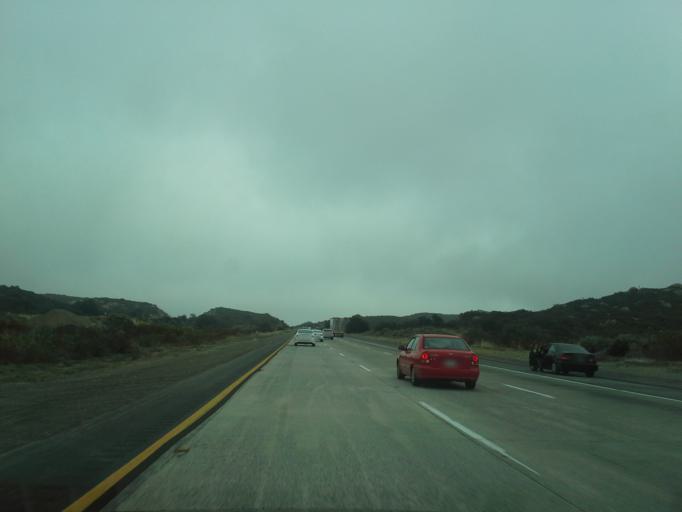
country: US
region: California
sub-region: San Diego County
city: Descanso
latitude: 32.8217
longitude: -116.5951
